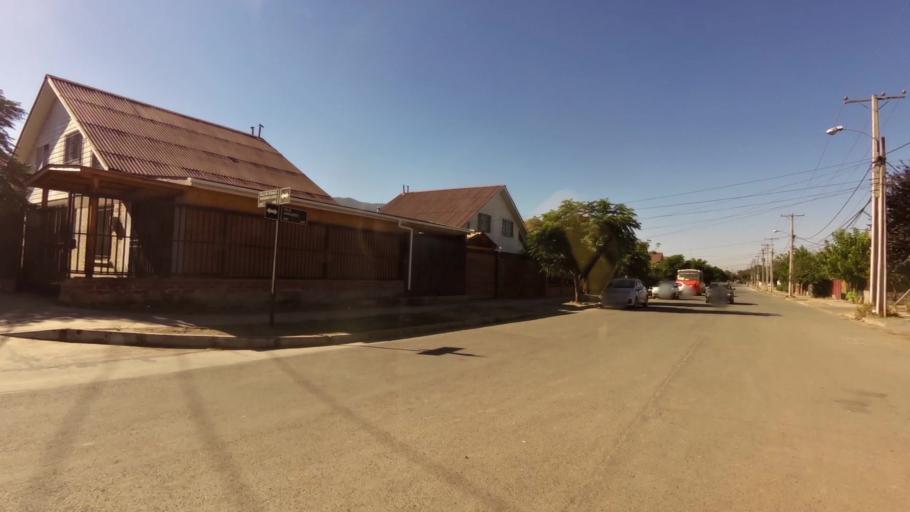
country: CL
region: O'Higgins
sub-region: Provincia de Colchagua
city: Chimbarongo
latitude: -34.5818
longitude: -71.0074
